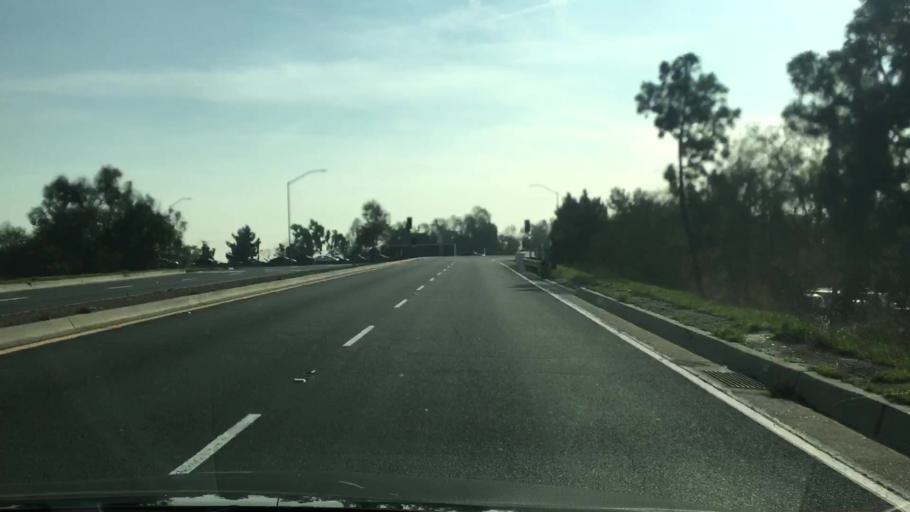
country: US
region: California
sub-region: Los Angeles County
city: Carson
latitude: 33.8270
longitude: -118.2266
